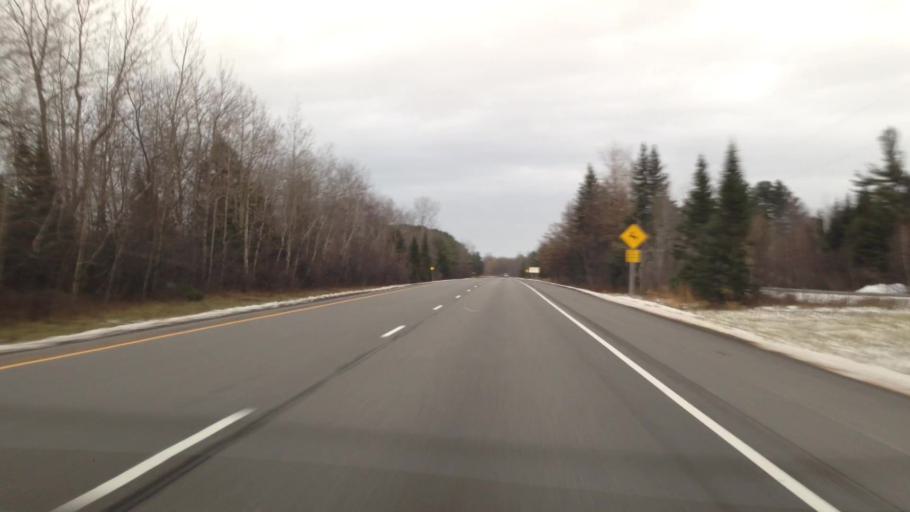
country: CA
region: Quebec
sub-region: Laurentides
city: Brownsburg-Chatham
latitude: 45.5514
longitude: -74.4428
